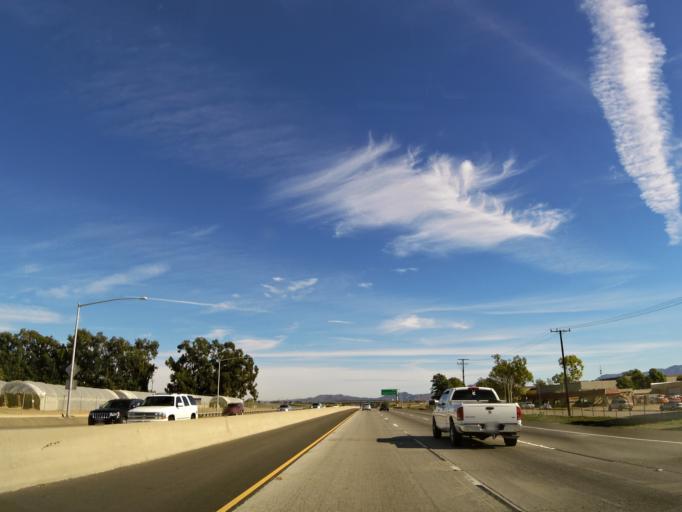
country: US
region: California
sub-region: Ventura County
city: Camarillo
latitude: 34.2211
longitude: -119.0941
